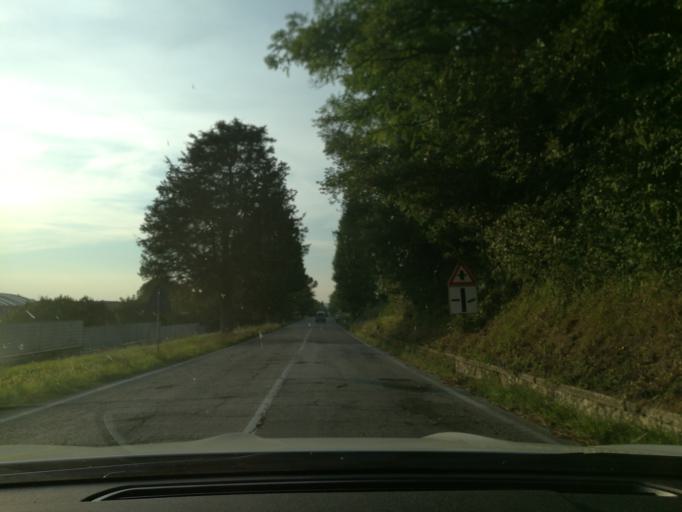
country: IT
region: Umbria
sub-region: Provincia di Terni
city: San Gemini
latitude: 42.6339
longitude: 12.5507
